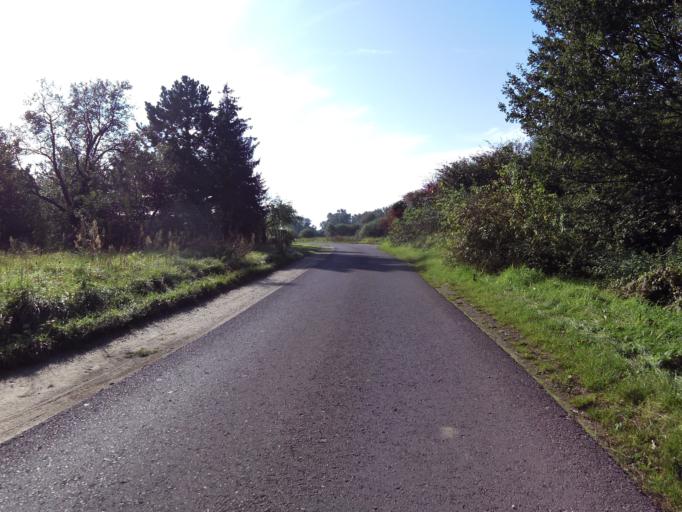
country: DE
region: Saxony-Anhalt
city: Coswig
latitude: 51.8773
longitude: 12.4674
